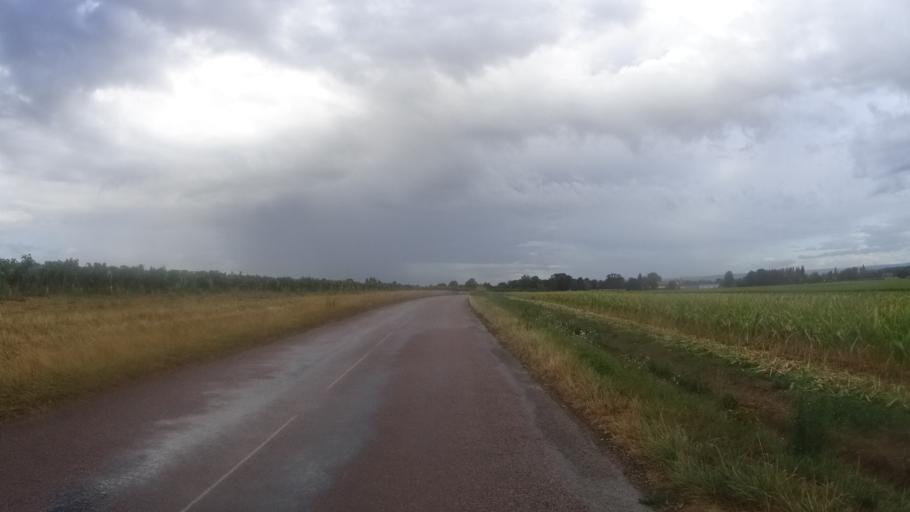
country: FR
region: Bourgogne
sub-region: Departement de Saone-et-Loire
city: Gergy
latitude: 46.9472
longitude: 4.9238
